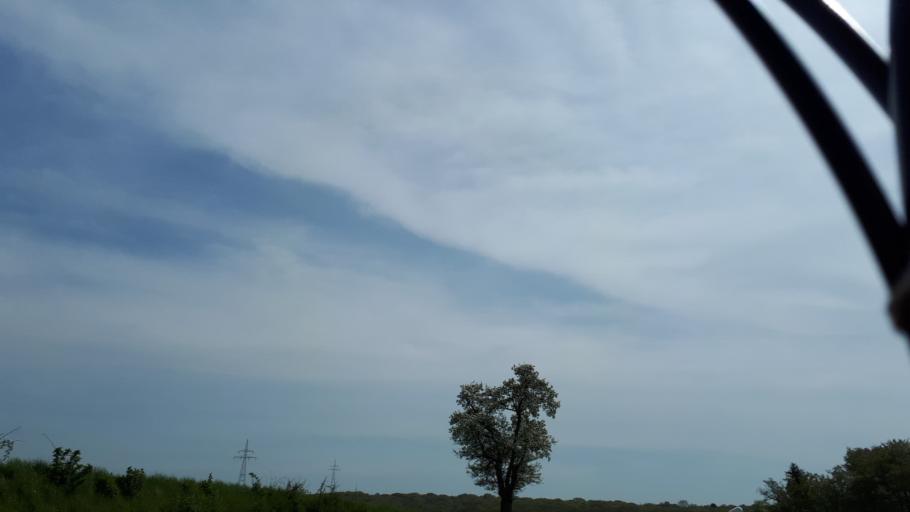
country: LU
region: Luxembourg
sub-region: Canton de Luxembourg
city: Bertrange
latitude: 49.5951
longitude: 6.0589
